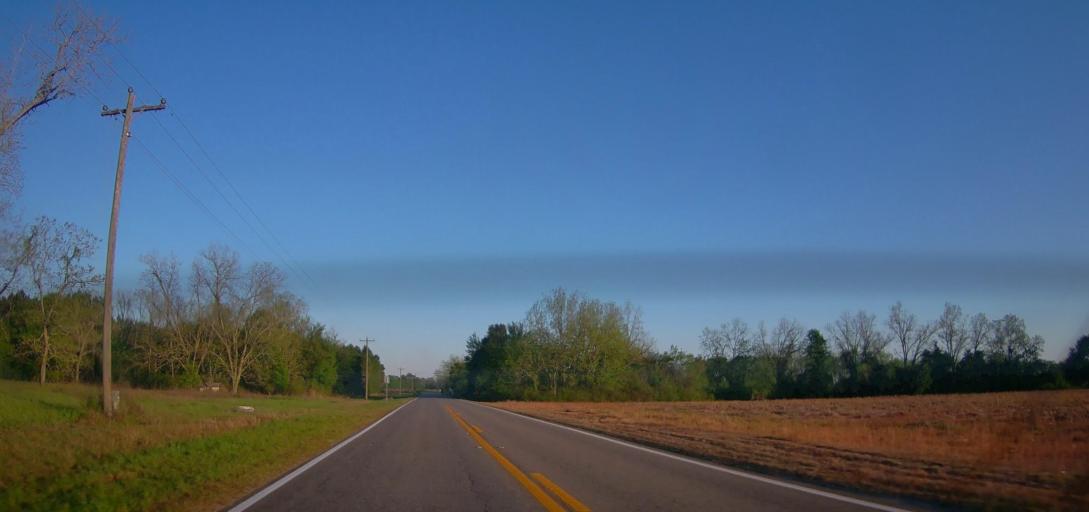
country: US
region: Georgia
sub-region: Irwin County
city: Ocilla
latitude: 31.6119
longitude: -83.2627
